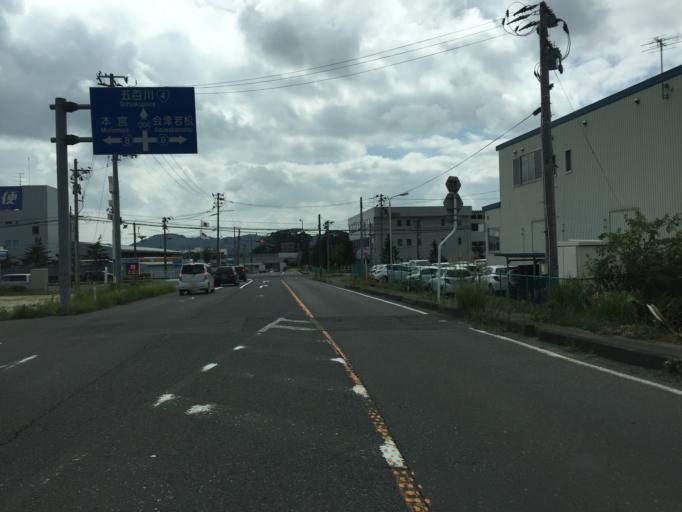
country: JP
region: Fukushima
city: Motomiya
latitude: 37.4877
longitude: 140.3731
